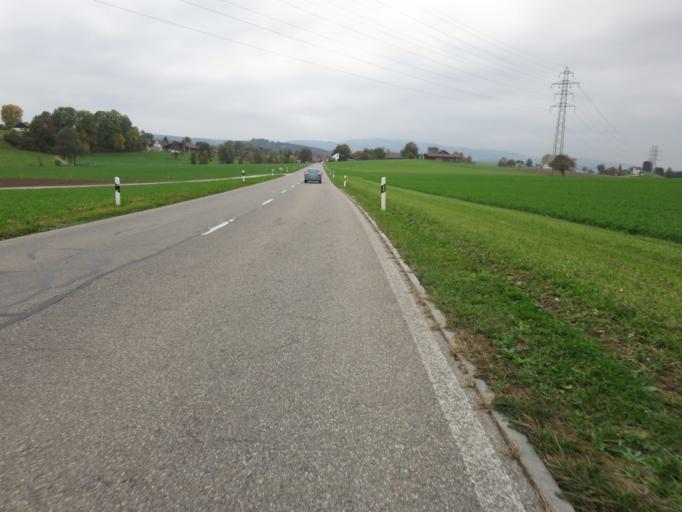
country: CH
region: Zurich
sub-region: Bezirk Hinwil
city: Binzikon
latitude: 47.2830
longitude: 8.7827
